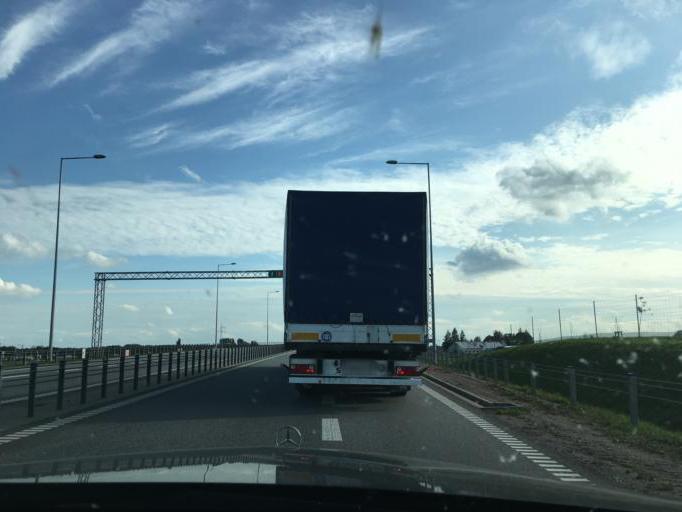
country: PL
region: Podlasie
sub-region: Powiat augustowski
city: Augustow
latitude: 53.8362
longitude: 22.9573
